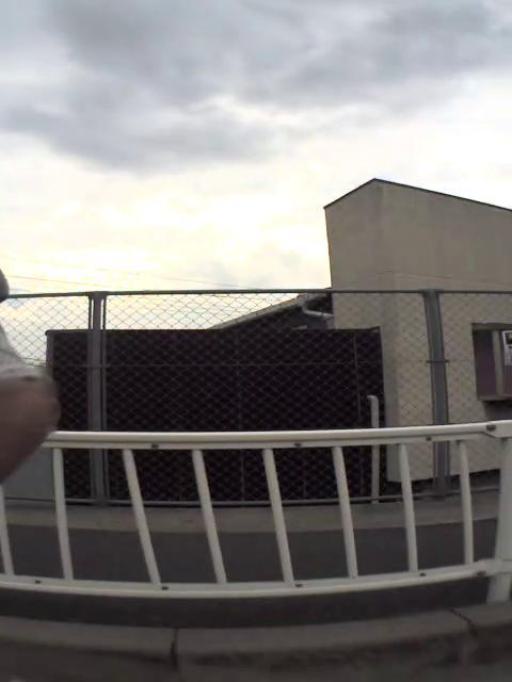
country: JP
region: Osaka
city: Neyagawa
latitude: 34.7804
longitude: 135.6322
